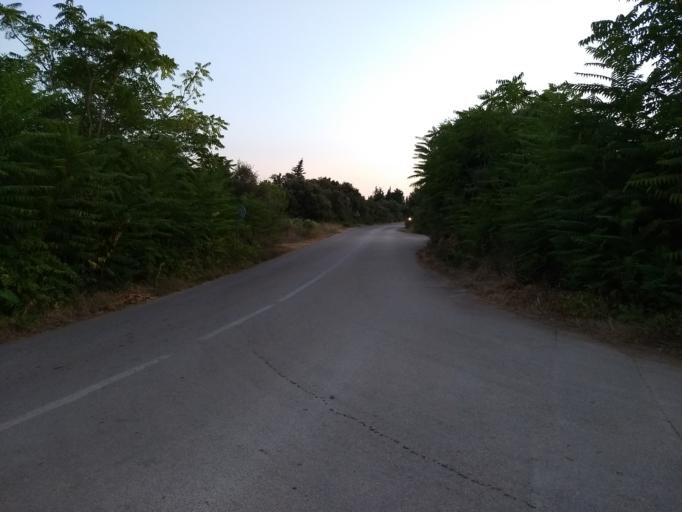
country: HR
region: Zadarska
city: Ugljan
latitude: 44.1421
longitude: 15.0839
